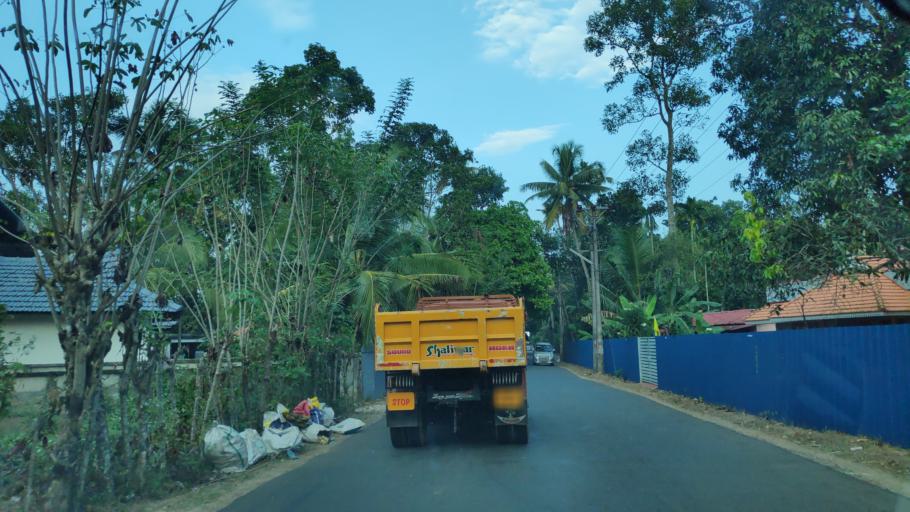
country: IN
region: Kerala
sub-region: Alappuzha
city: Shertallai
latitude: 9.6624
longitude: 76.3813
